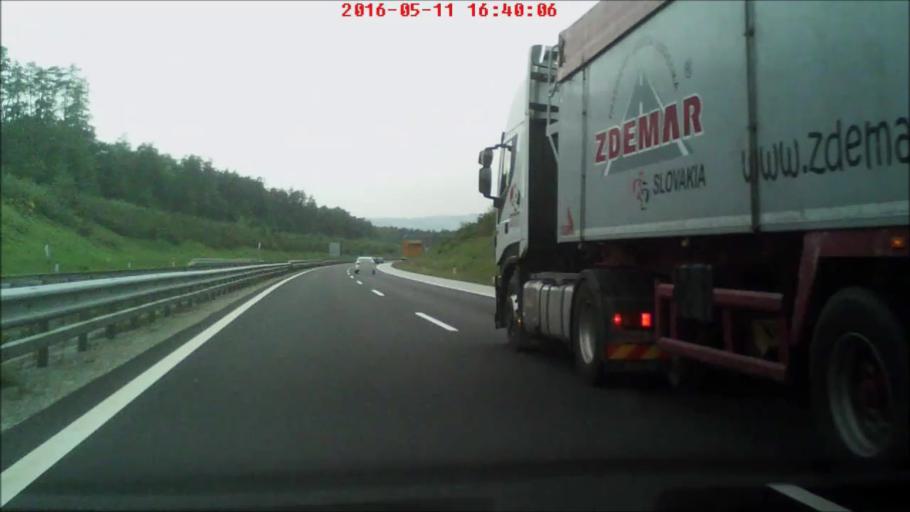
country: SI
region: Miklavz na Dravskem Polju
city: Miklavz na Dravskem Polju
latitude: 46.5241
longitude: 15.6948
